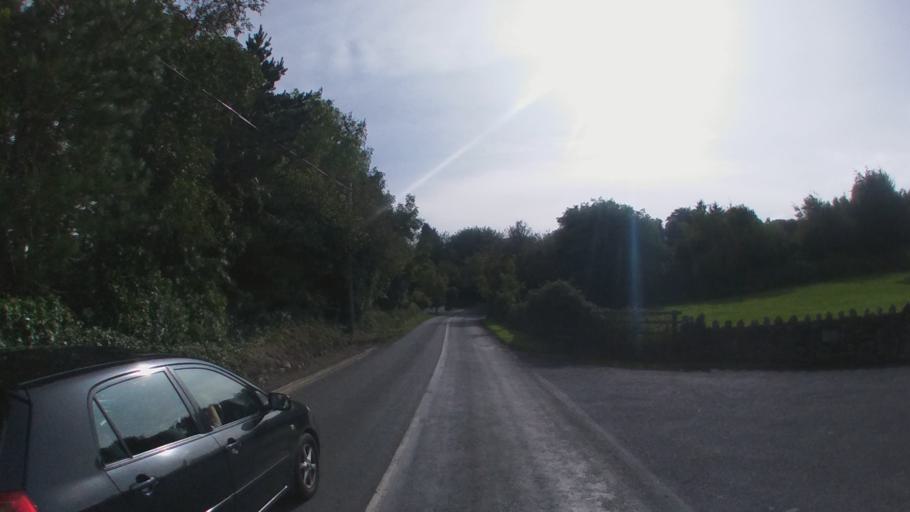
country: IE
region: Leinster
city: Sandyford
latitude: 53.2348
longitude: -6.2215
